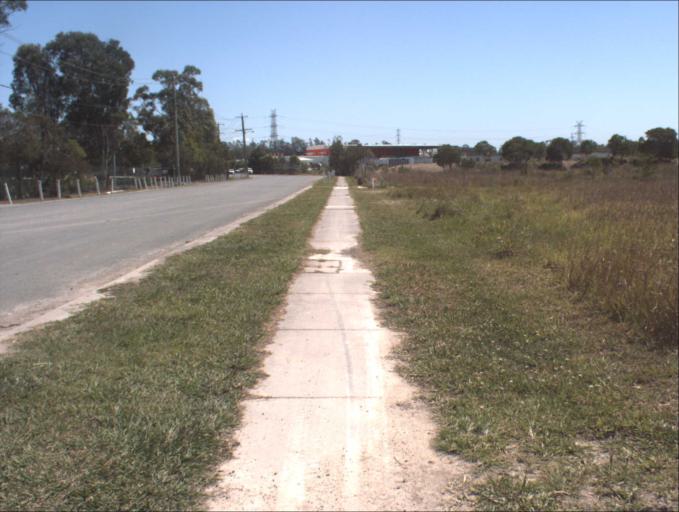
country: AU
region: Queensland
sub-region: Logan
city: Waterford West
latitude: -27.6739
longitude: 153.1166
